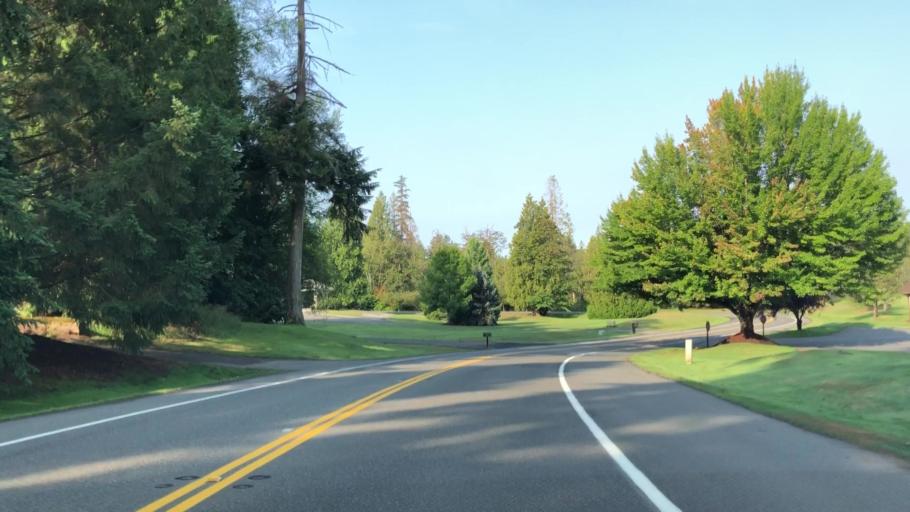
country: US
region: Washington
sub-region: King County
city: Cottage Lake
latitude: 47.7216
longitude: -122.0668
